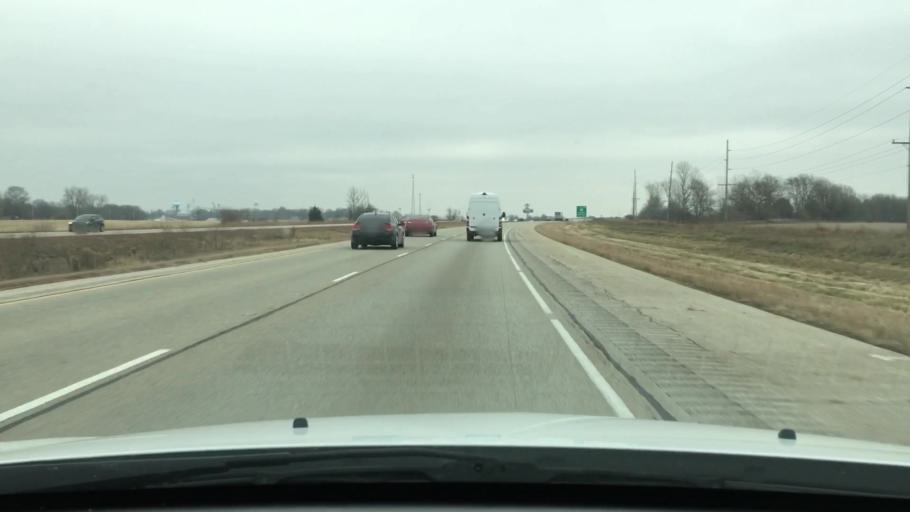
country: US
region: Illinois
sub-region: Logan County
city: Atlanta
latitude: 40.3030
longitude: -89.1810
